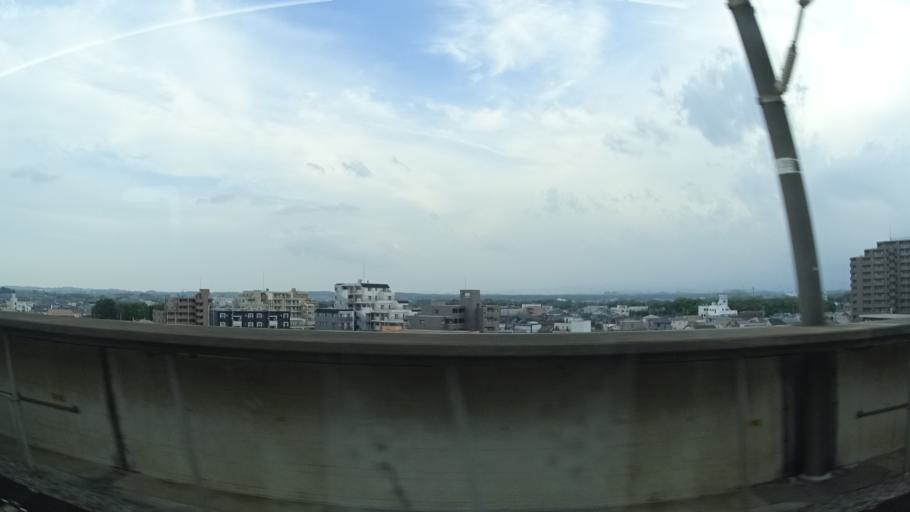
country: JP
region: Saitama
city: Kumagaya
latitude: 36.1383
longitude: 139.3927
